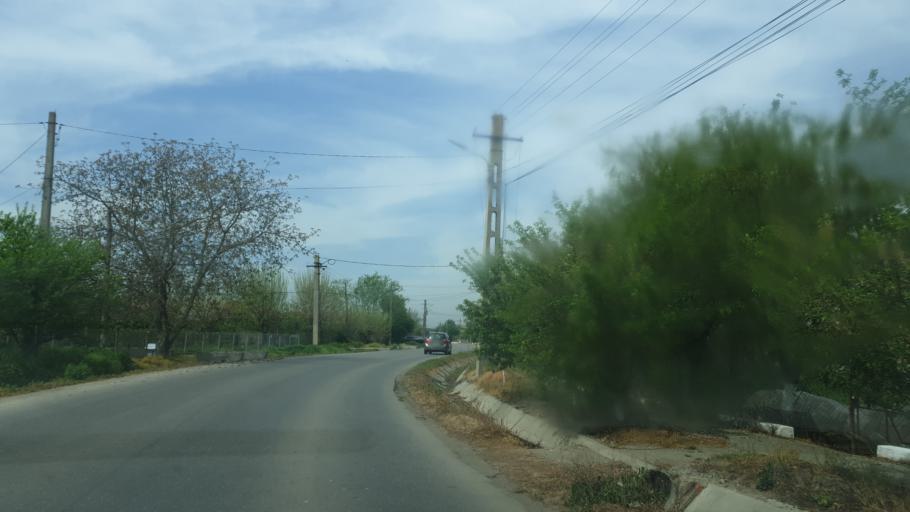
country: RO
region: Giurgiu
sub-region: Comuna Hotarele
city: Hotarele
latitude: 44.1783
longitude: 26.3847
